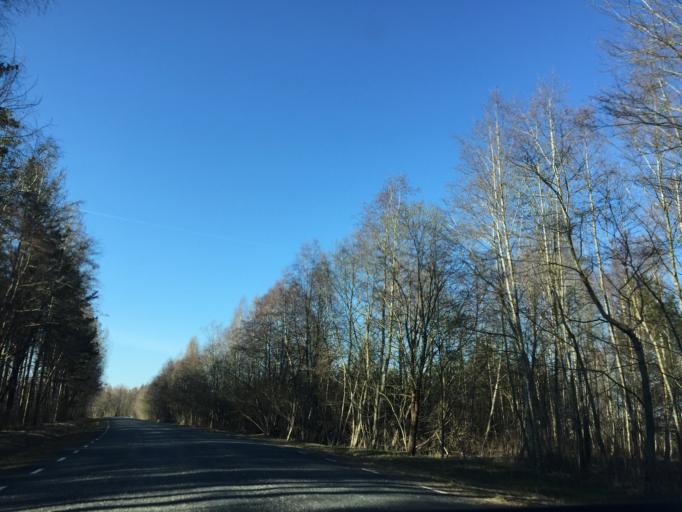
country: RU
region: Pskov
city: Gdov
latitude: 59.0302
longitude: 27.6882
